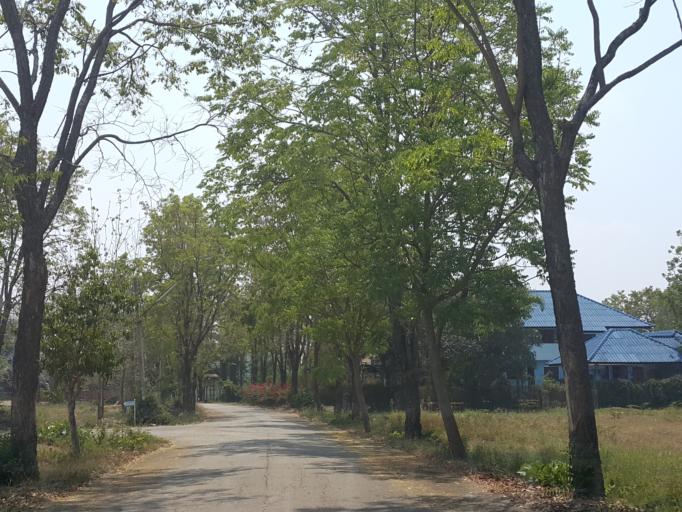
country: TH
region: Chiang Mai
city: Saraphi
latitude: 18.7275
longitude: 98.9778
